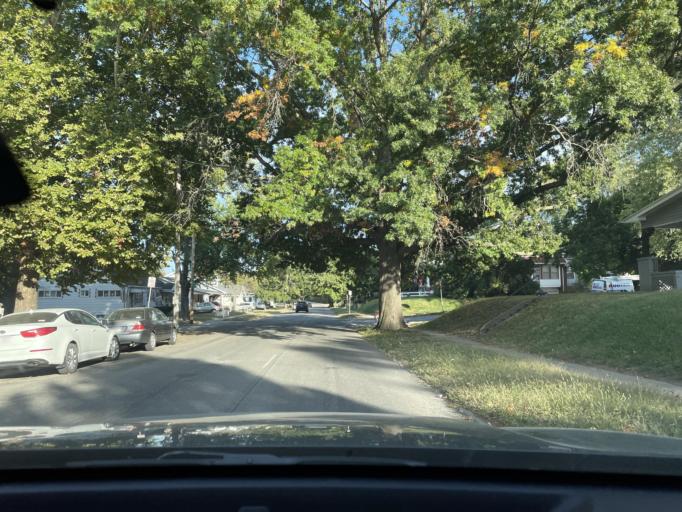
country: US
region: Missouri
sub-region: Buchanan County
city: Saint Joseph
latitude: 39.7683
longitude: -94.8184
